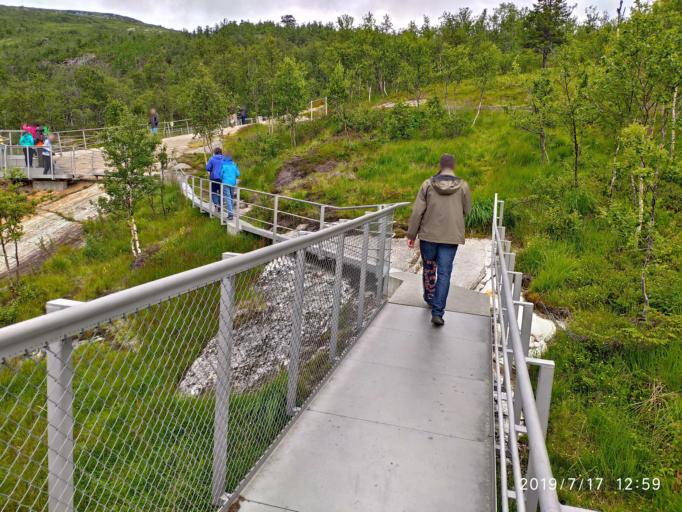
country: NO
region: Hordaland
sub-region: Eidfjord
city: Eidfjord
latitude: 60.4279
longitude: 7.2536
